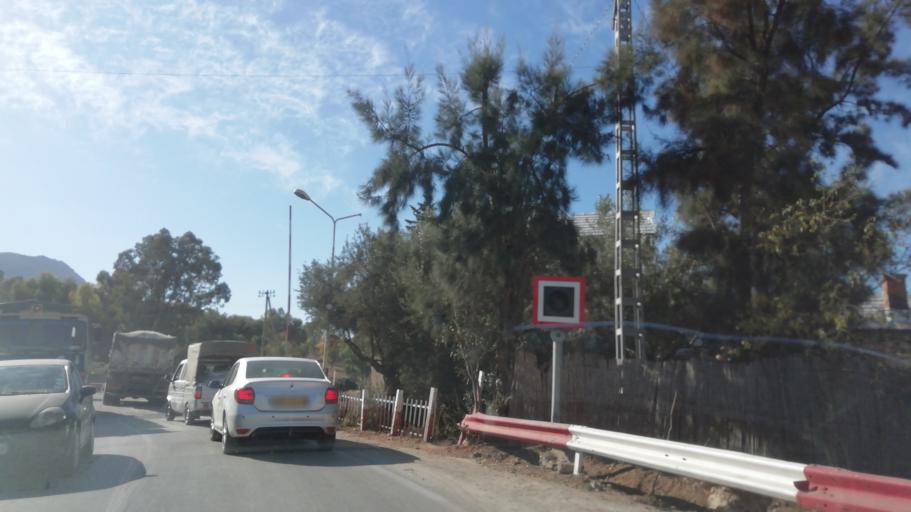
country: DZ
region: Tlemcen
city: Ouled Mimoun
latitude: 34.8982
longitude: -1.0538
